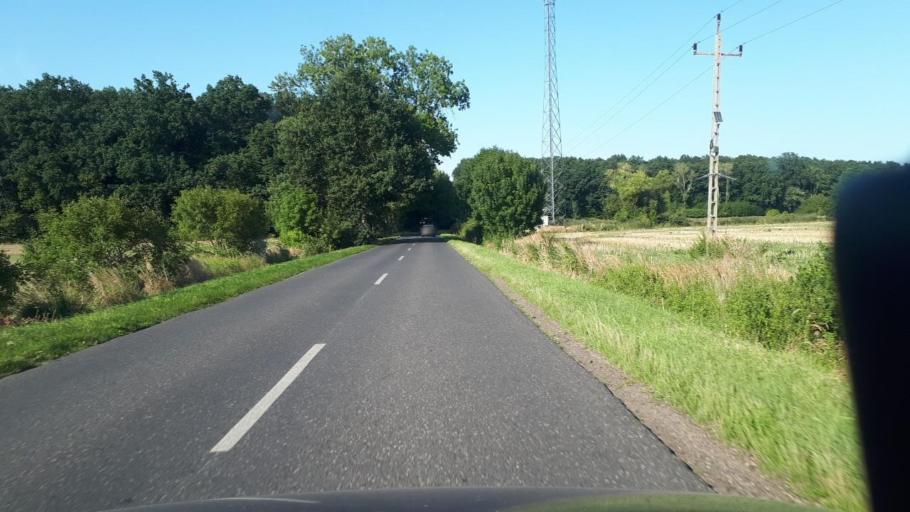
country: PL
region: Silesian Voivodeship
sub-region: Powiat tarnogorski
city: Tworog
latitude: 50.4758
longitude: 18.6832
